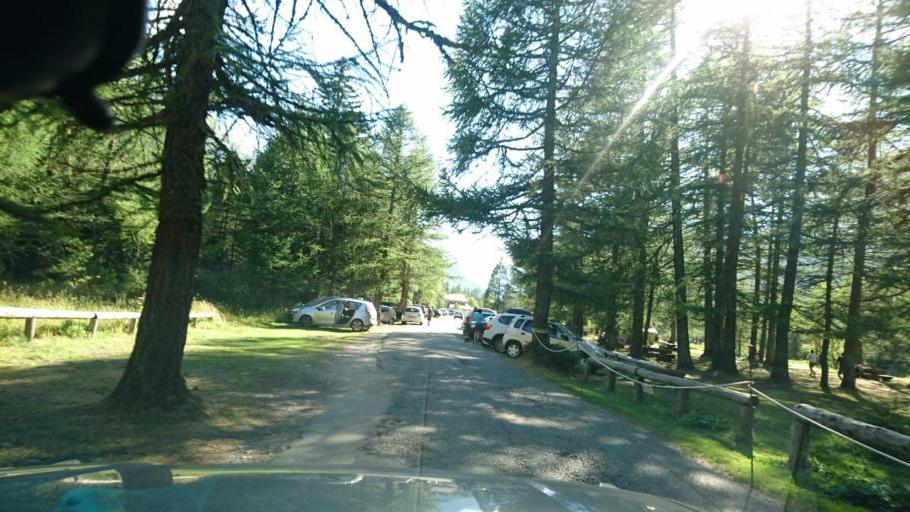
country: IT
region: Aosta Valley
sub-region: Valle d'Aosta
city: Courmayeur
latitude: 45.8521
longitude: 7.0246
